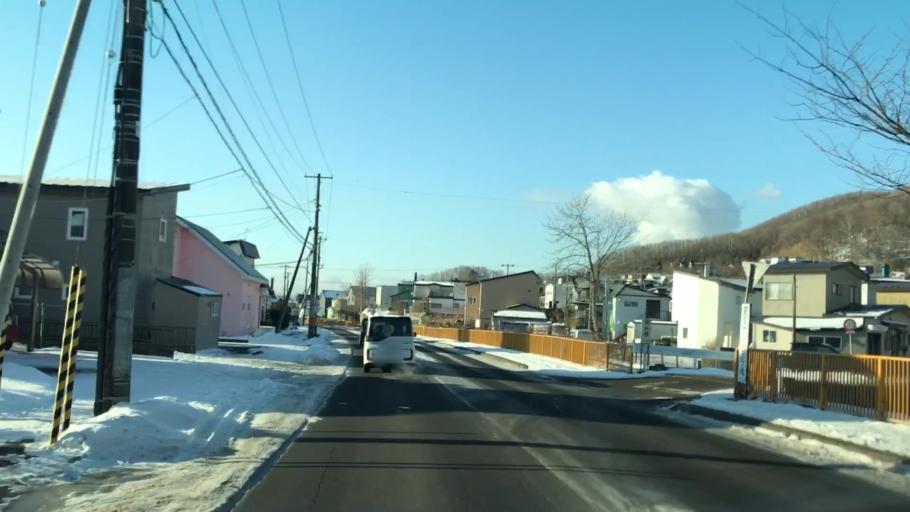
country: JP
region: Hokkaido
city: Muroran
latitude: 42.3706
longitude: 141.0522
